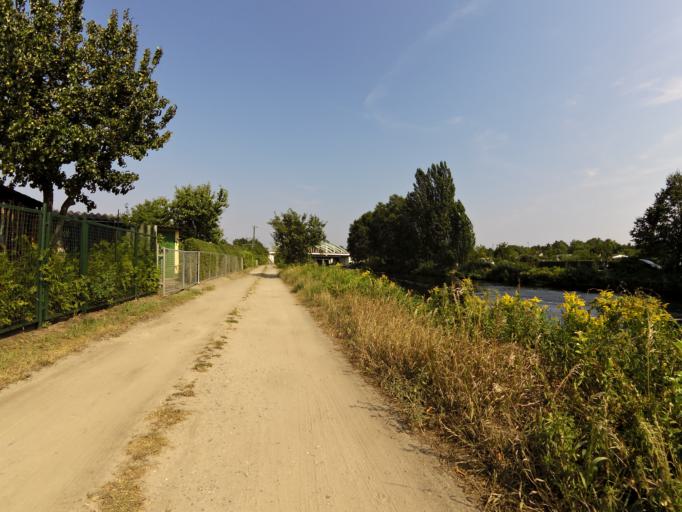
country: DE
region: Berlin
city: Adlershof
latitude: 52.4257
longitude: 13.5515
